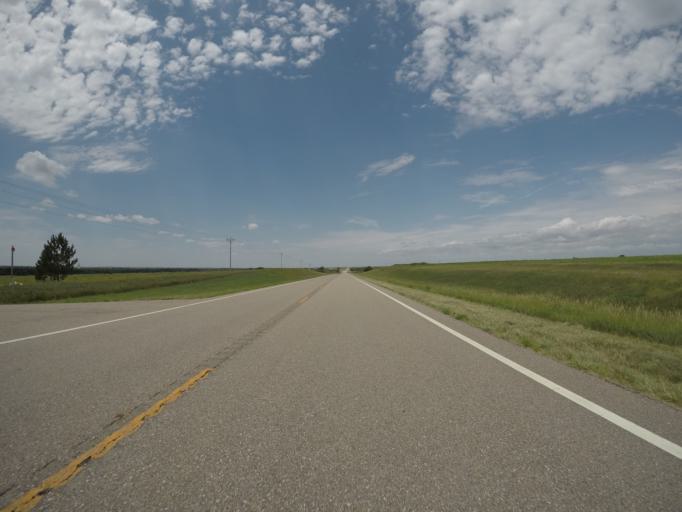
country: US
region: Kansas
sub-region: Graham County
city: Hill City
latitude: 39.3798
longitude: -99.6709
